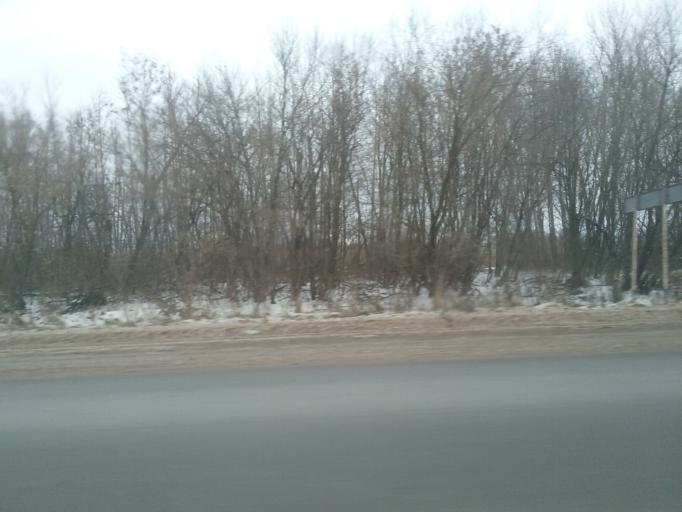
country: RU
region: Tula
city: Bolokhovo
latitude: 54.0935
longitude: 37.7702
